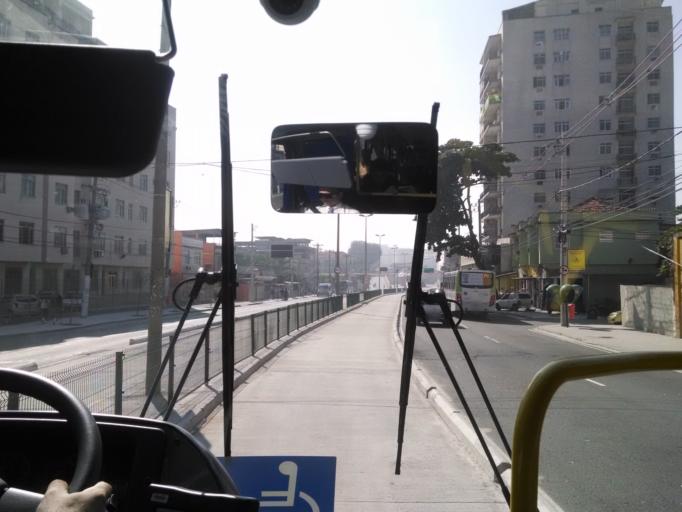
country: BR
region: Rio de Janeiro
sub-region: Duque De Caxias
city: Duque de Caxias
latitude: -22.8546
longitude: -43.3229
